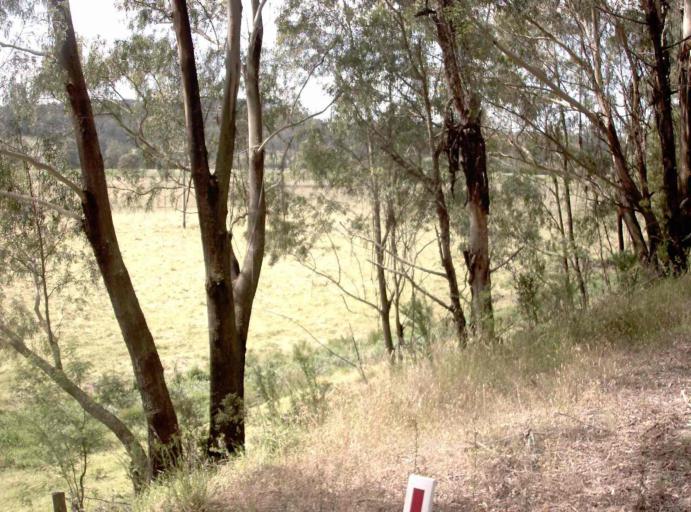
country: AU
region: New South Wales
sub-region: Bega Valley
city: Eden
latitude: -37.4801
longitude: 149.6074
